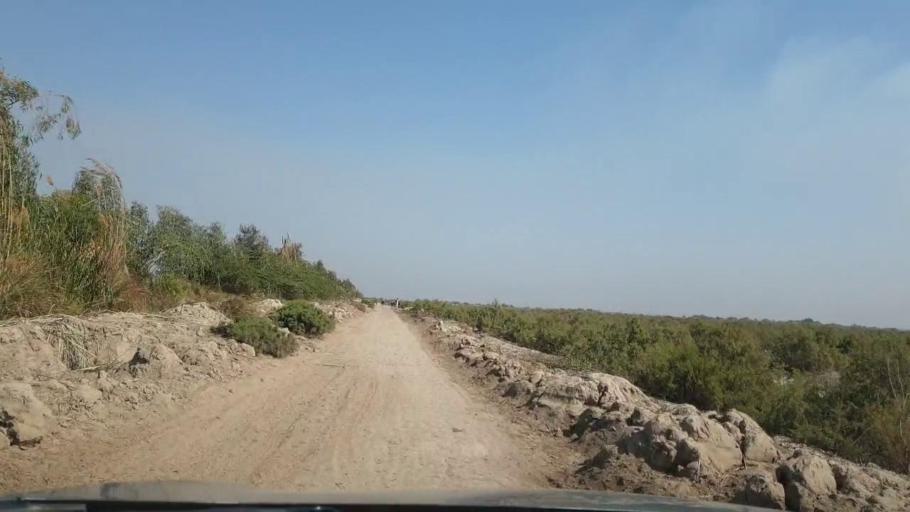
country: PK
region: Sindh
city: Berani
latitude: 25.6526
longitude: 68.8791
